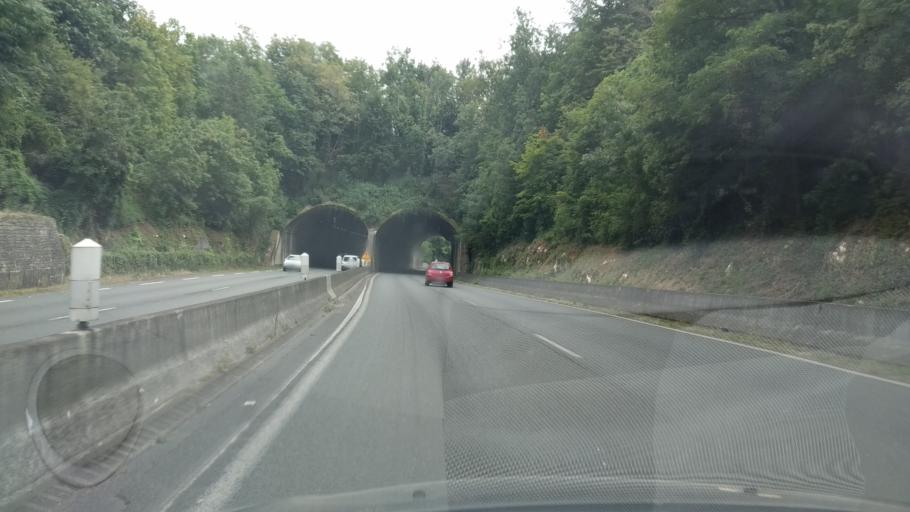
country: FR
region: Poitou-Charentes
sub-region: Departement de la Vienne
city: Saint-Benoit
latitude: 46.5603
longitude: 0.3402
